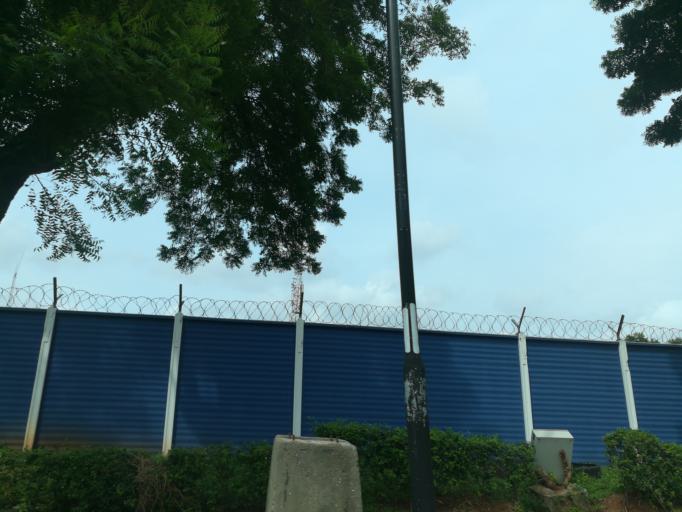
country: NG
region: Lagos
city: Ojota
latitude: 6.6040
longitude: 3.3720
